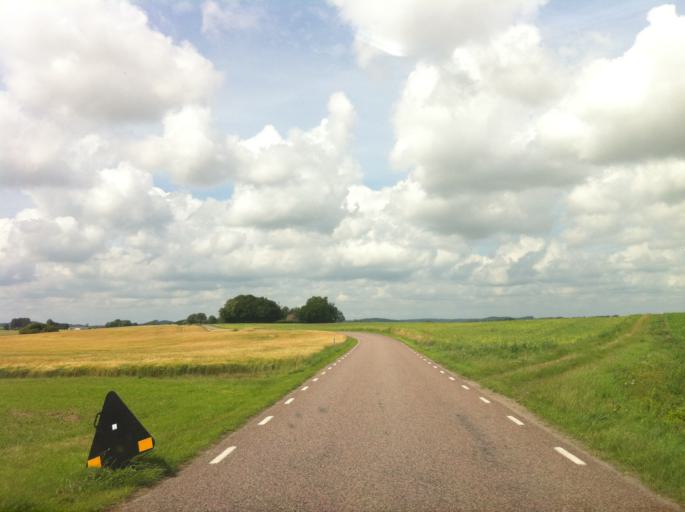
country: SE
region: Skane
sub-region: Skurups Kommun
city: Skurup
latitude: 55.4200
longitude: 13.4568
